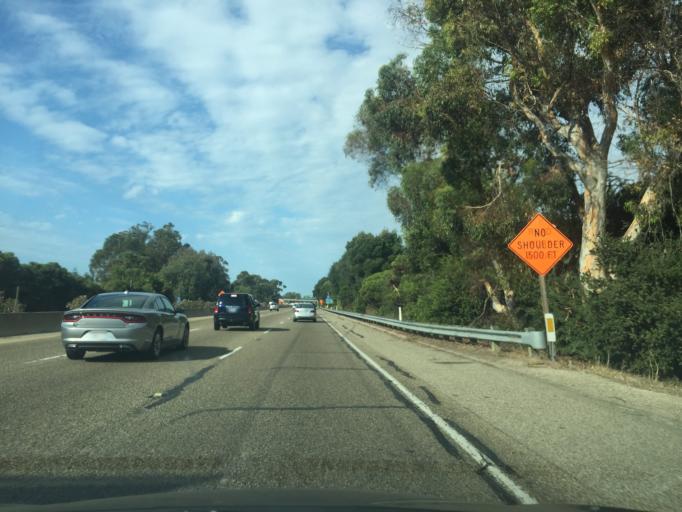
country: US
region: California
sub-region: Santa Barbara County
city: Goleta
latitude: 34.4407
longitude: -119.8213
